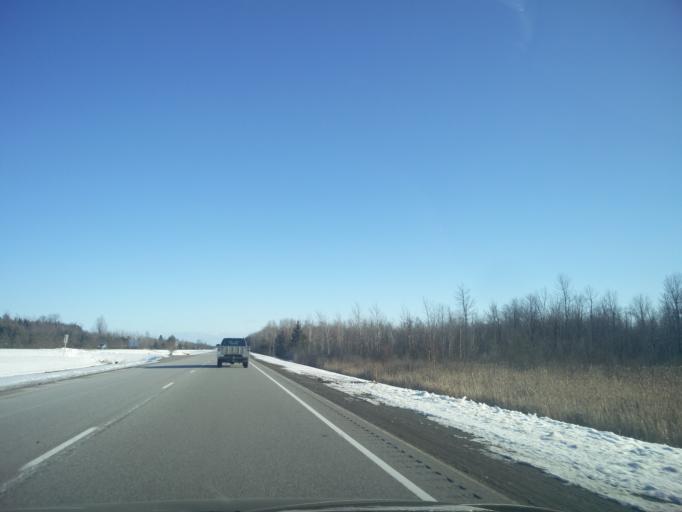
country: CA
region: Ontario
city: Prescott
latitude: 44.9712
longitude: -75.6032
